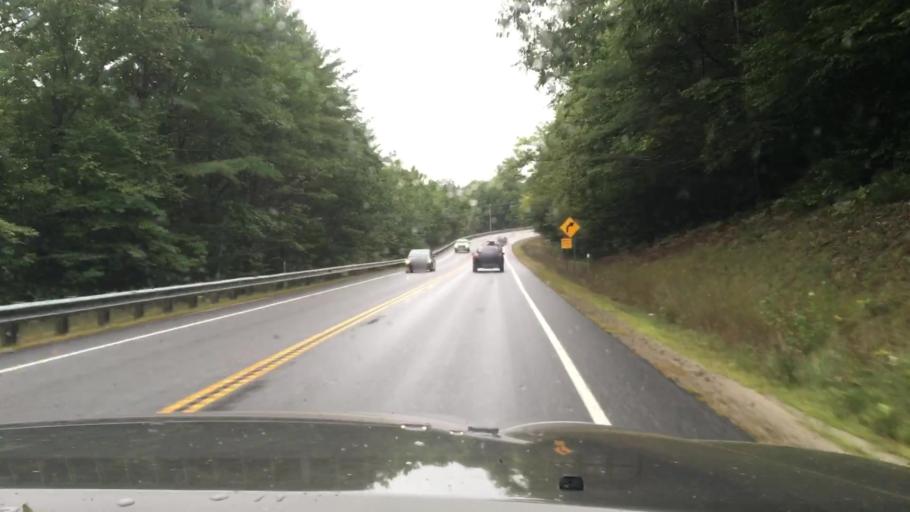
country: US
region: New Hampshire
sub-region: Hillsborough County
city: Antrim
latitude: 43.0683
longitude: -72.0542
